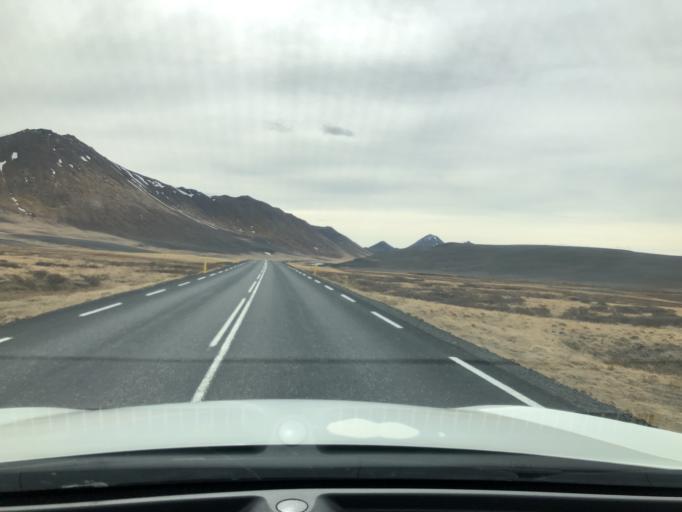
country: IS
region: Northeast
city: Laugar
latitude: 65.4851
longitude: -15.9640
